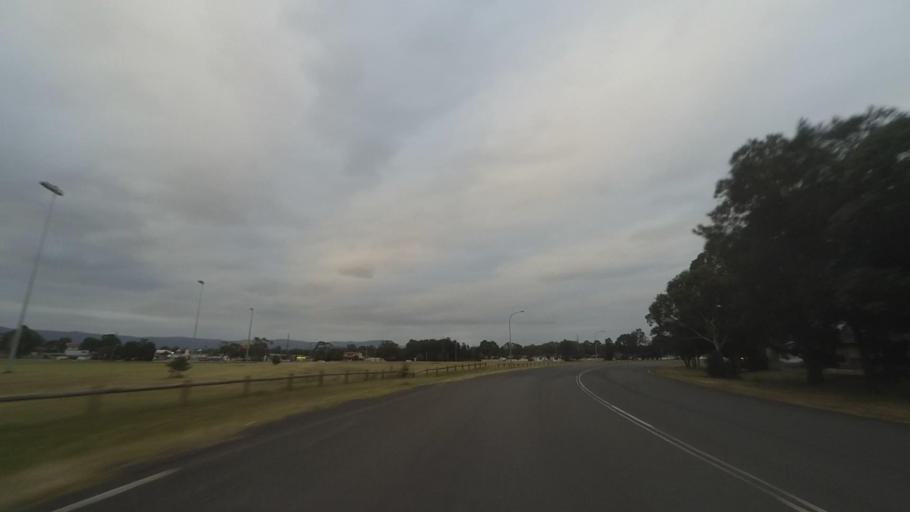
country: AU
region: New South Wales
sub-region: Shellharbour
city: Albion Park Rail
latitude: -34.5708
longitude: 150.8039
